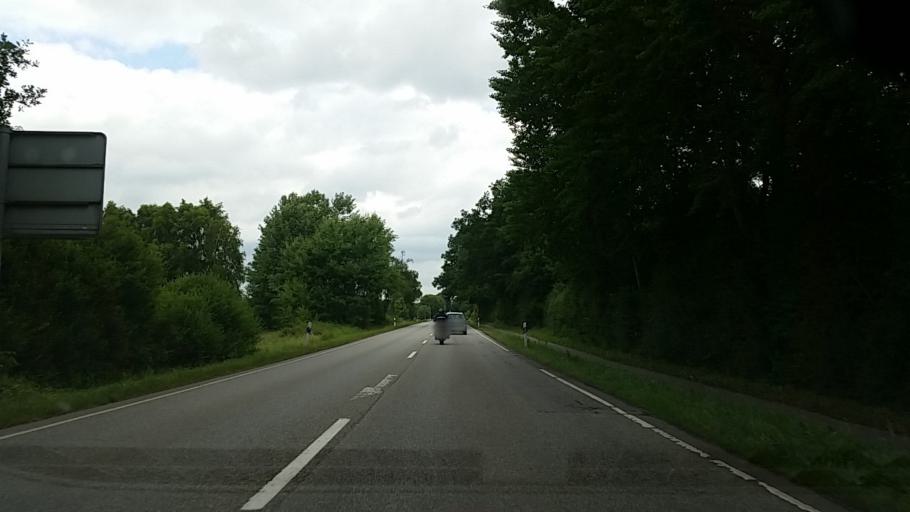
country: DE
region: Schleswig-Holstein
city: Tangstedt
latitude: 53.7155
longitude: 10.0797
